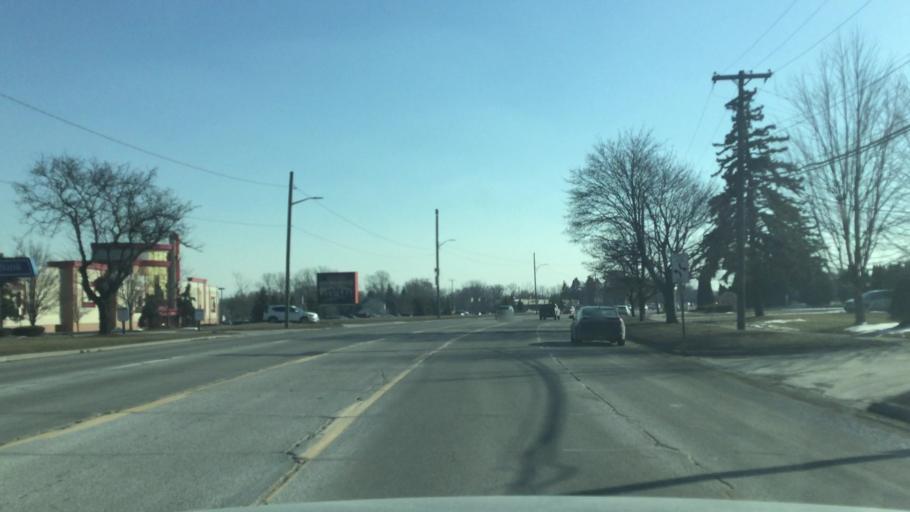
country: US
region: Michigan
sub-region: Wayne County
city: Westland
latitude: 42.3361
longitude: -83.3849
